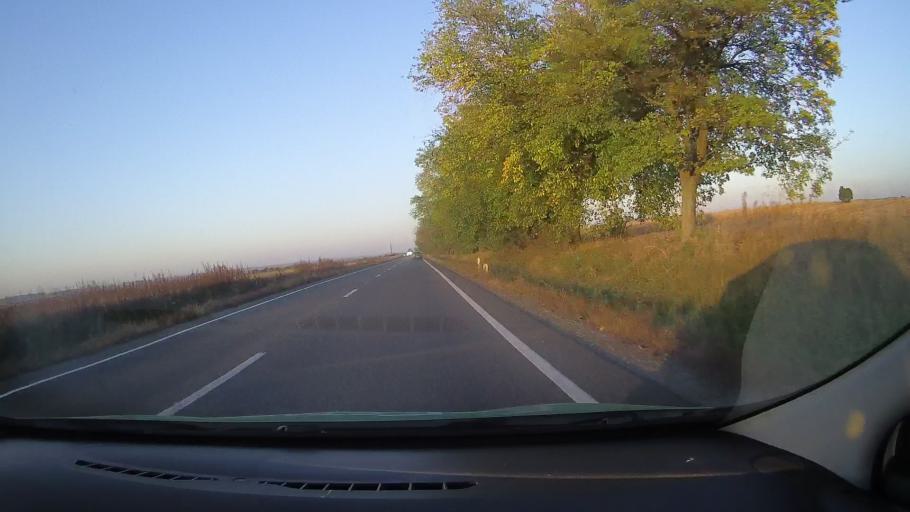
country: RO
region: Bihor
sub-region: Comuna Rosiori
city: Rosiori
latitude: 47.2698
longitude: 21.9748
